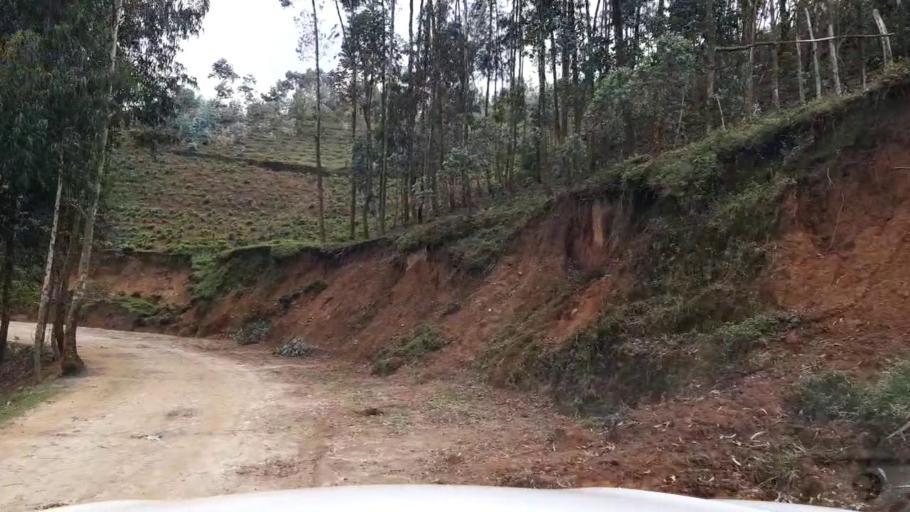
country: RW
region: Western Province
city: Kibuye
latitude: -1.9568
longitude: 29.4768
